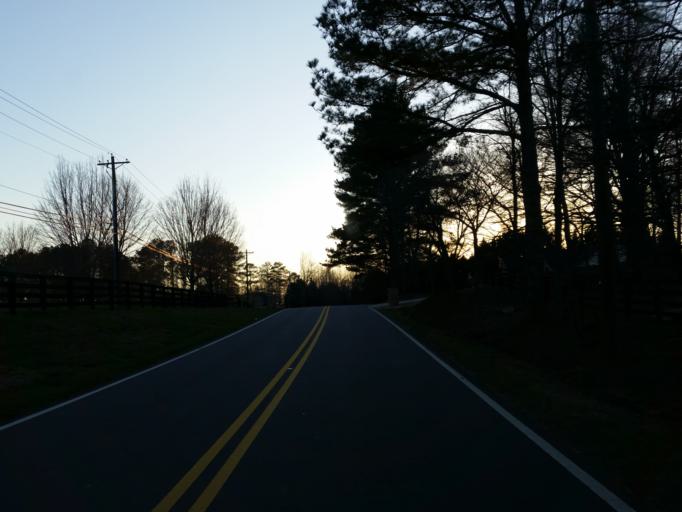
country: US
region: Georgia
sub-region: Cherokee County
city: Holly Springs
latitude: 34.1242
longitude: -84.4291
